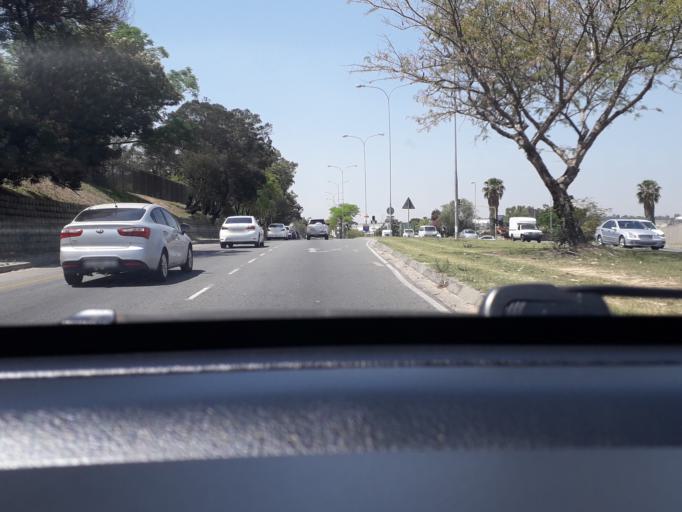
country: ZA
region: Gauteng
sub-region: City of Johannesburg Metropolitan Municipality
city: Modderfontein
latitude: -26.0849
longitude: 28.1023
